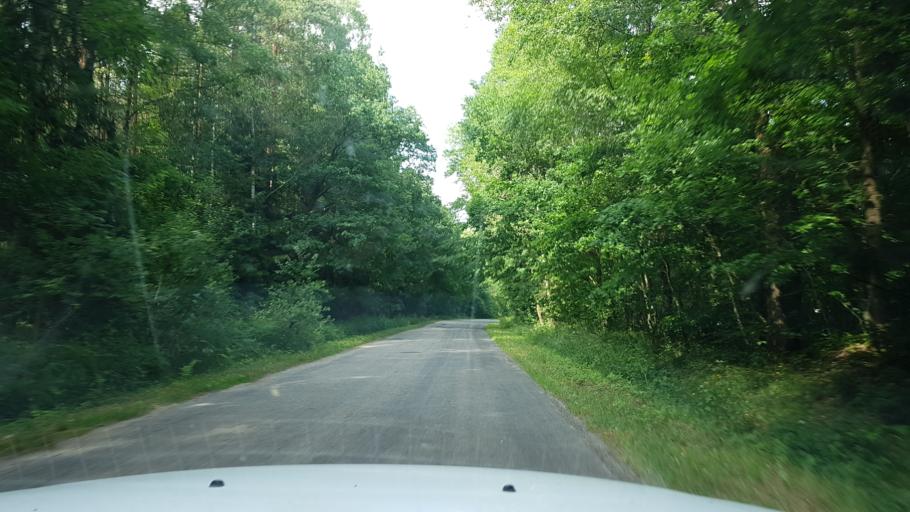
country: PL
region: West Pomeranian Voivodeship
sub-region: Powiat goleniowski
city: Osina
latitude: 53.5862
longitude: 14.9872
